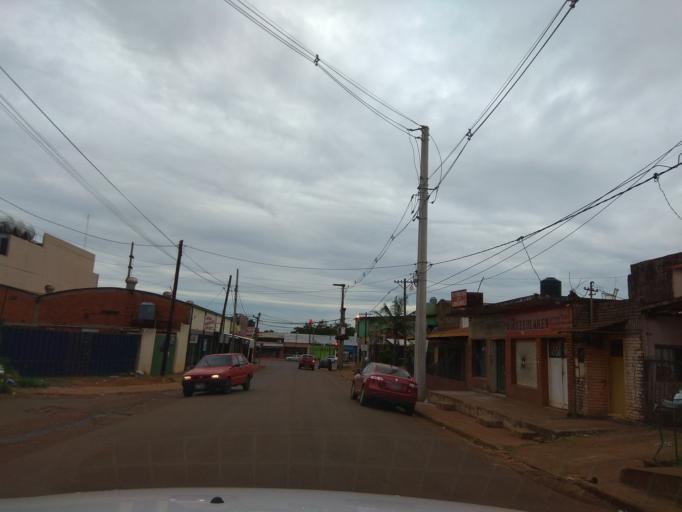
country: AR
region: Misiones
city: Garupa
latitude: -27.4454
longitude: -55.8714
